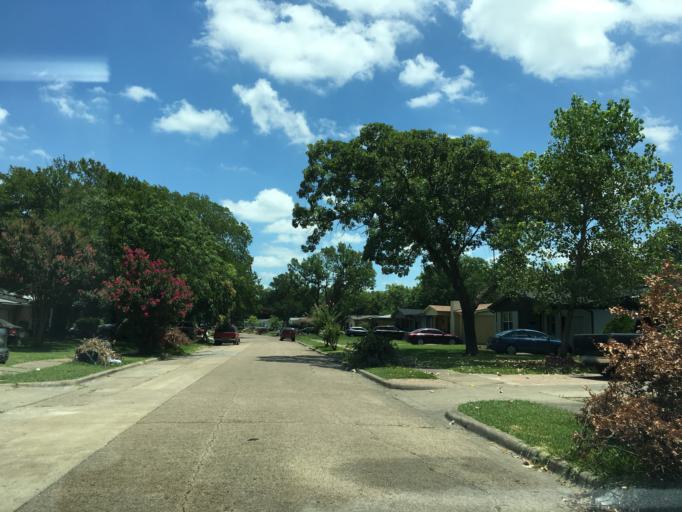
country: US
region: Texas
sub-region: Dallas County
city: Garland
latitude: 32.8366
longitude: -96.6645
